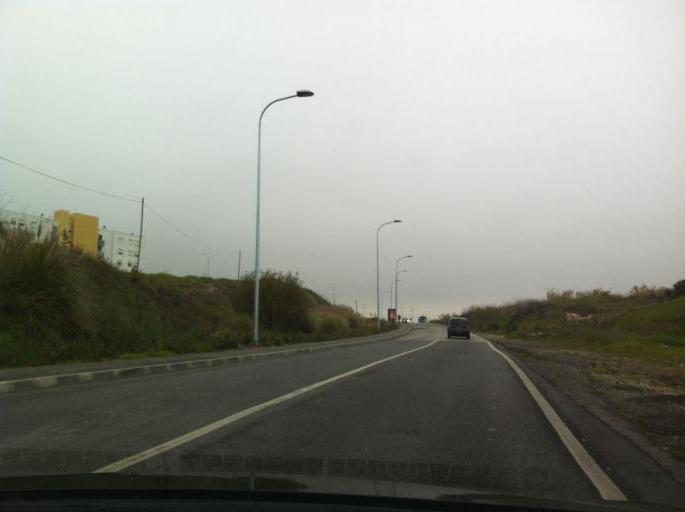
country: PT
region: Lisbon
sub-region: Odivelas
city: Famoes
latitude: 38.7812
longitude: -9.2206
